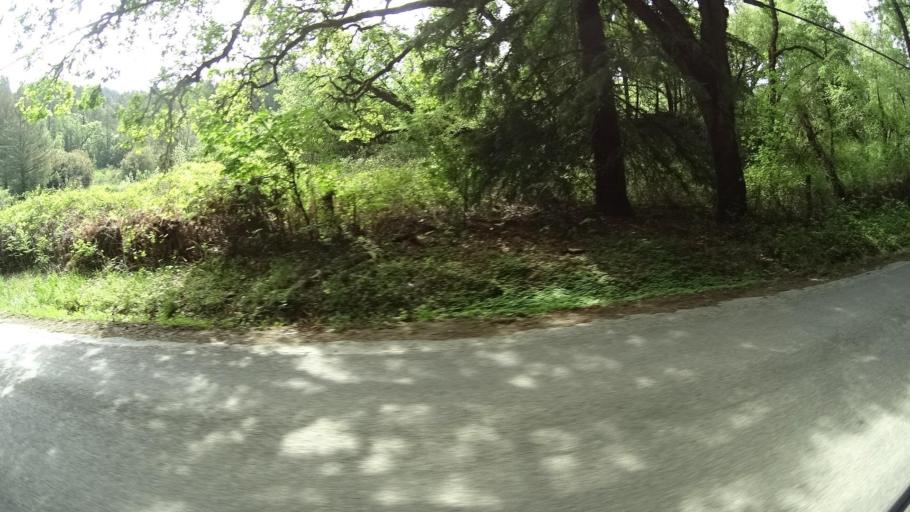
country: US
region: California
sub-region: Humboldt County
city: Redway
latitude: 40.0895
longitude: -123.7958
